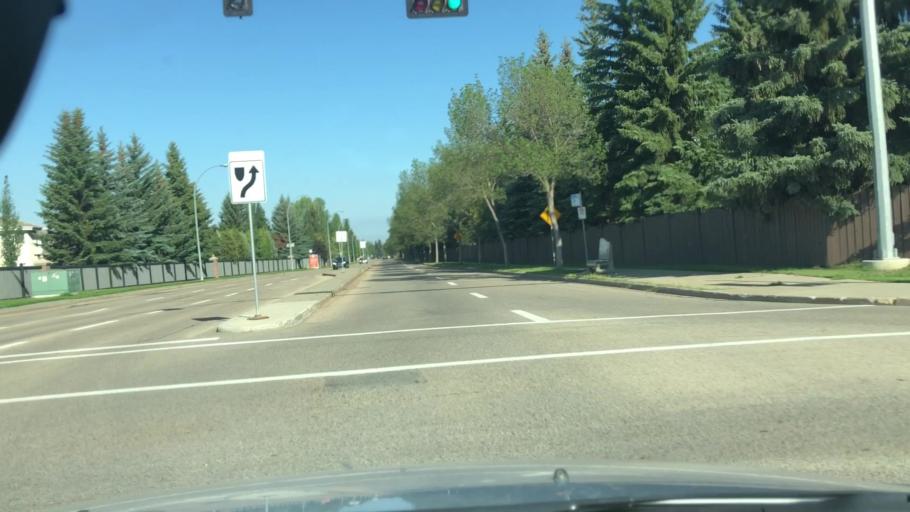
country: CA
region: Alberta
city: Edmonton
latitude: 53.4722
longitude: -113.5941
